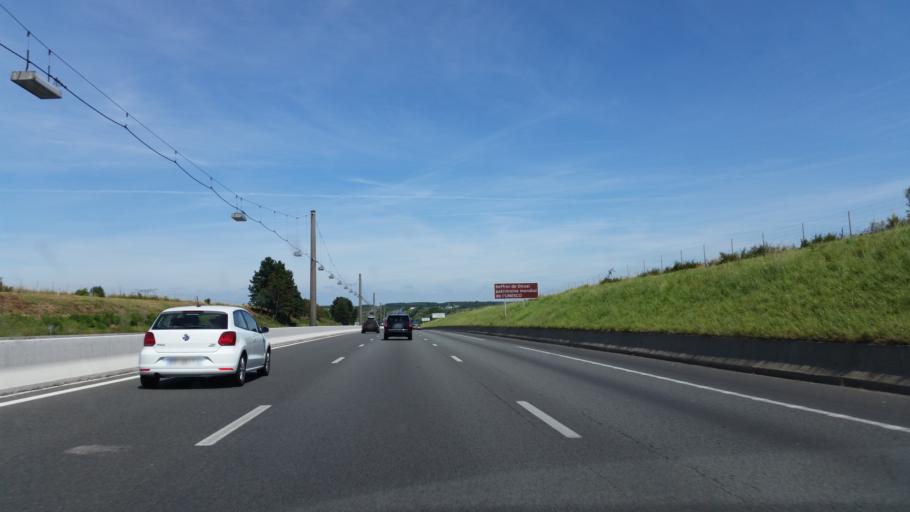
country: FR
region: Nord-Pas-de-Calais
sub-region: Departement du Pas-de-Calais
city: Fampoux
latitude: 50.2840
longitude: 2.8777
